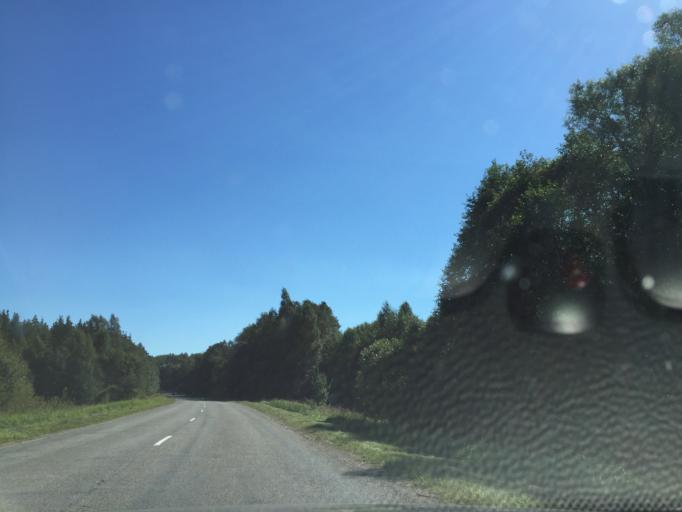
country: LV
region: Akniste
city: Akniste
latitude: 56.1198
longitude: 25.8315
